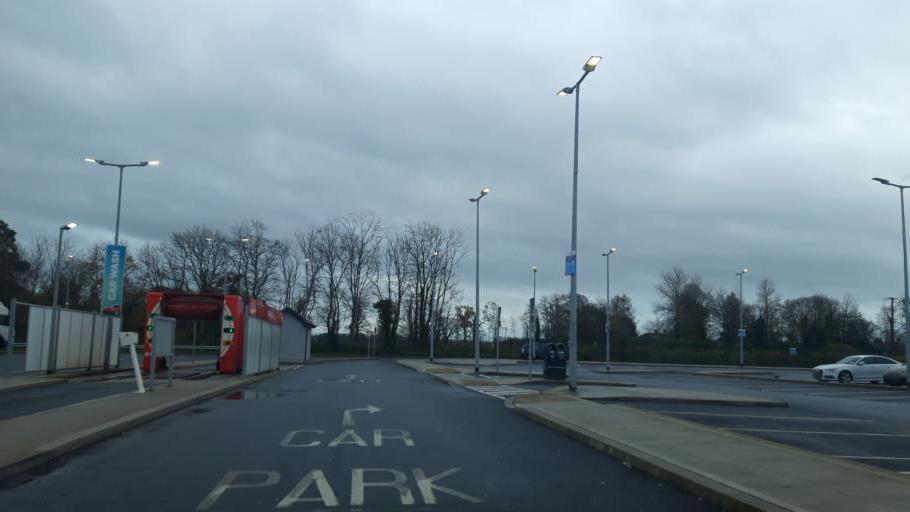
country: IE
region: Leinster
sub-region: County Carlow
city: Carlow
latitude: 52.8031
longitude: -6.8827
